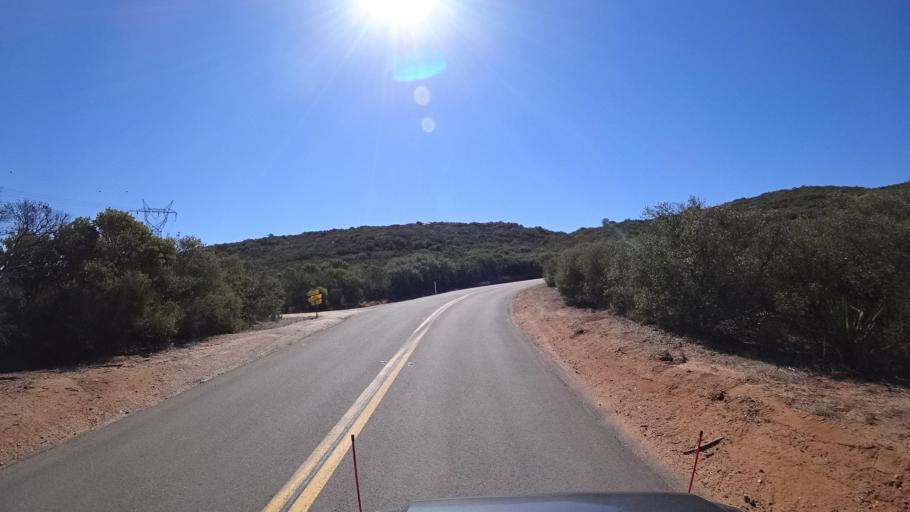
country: US
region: California
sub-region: San Diego County
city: Alpine
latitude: 32.7787
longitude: -116.7161
